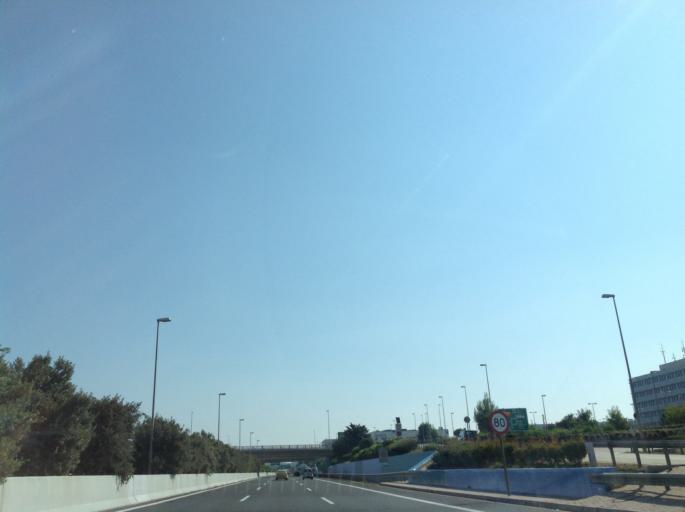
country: GR
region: Attica
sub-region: Nomarchia Anatolikis Attikis
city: Markopoulo
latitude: 37.9200
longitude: 23.9290
